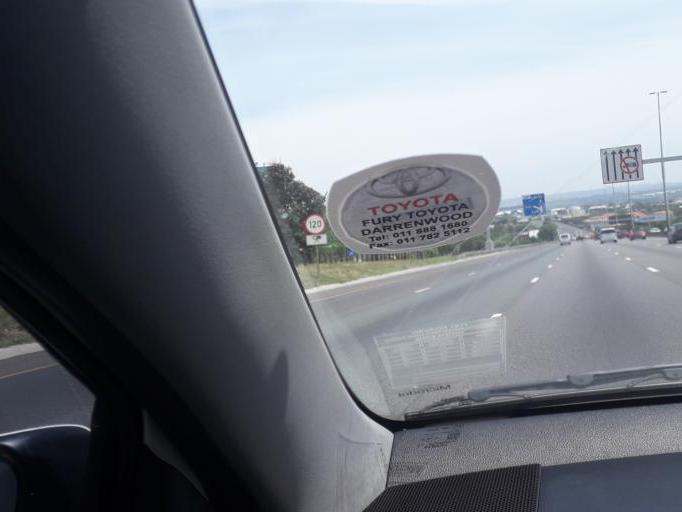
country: ZA
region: Gauteng
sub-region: City of Johannesburg Metropolitan Municipality
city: Midrand
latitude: -25.9866
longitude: 28.1244
